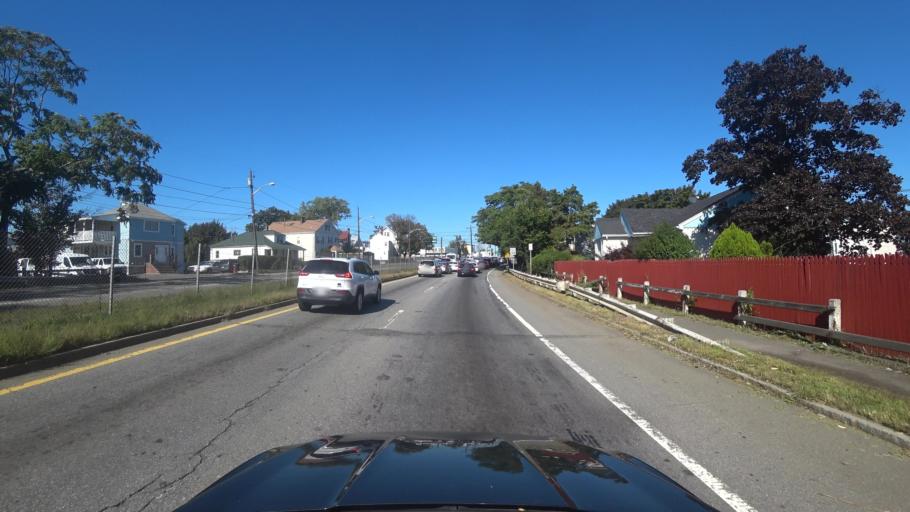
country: US
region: Massachusetts
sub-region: Suffolk County
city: Revere
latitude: 42.4152
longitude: -71.0036
